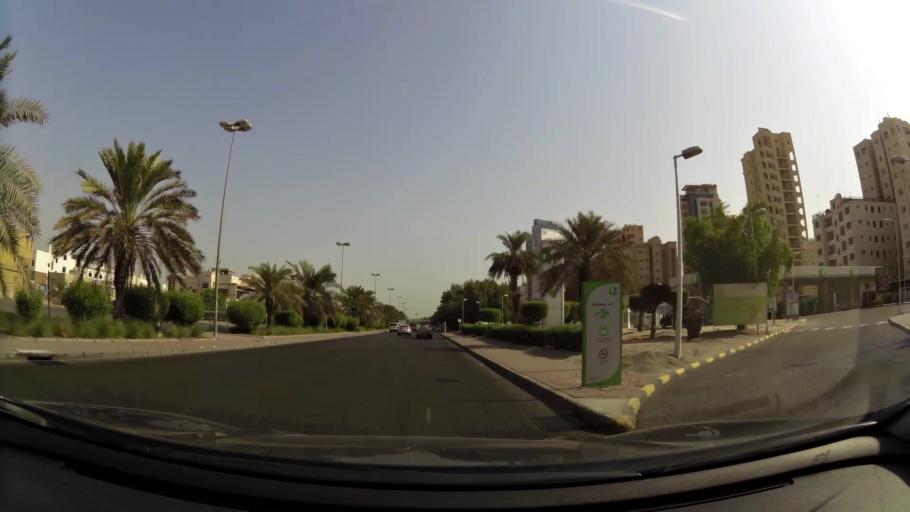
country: KW
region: Al Asimah
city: Ad Dasmah
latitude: 29.3454
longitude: 48.0085
